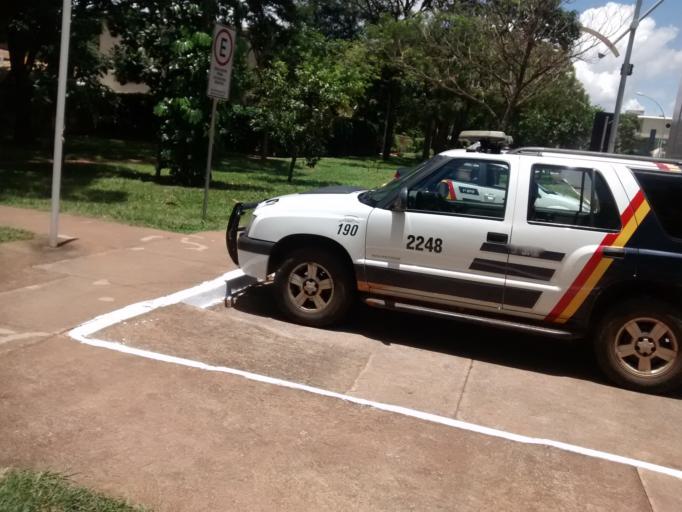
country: BR
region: Federal District
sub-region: Brasilia
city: Brasilia
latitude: -15.8196
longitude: -47.9207
